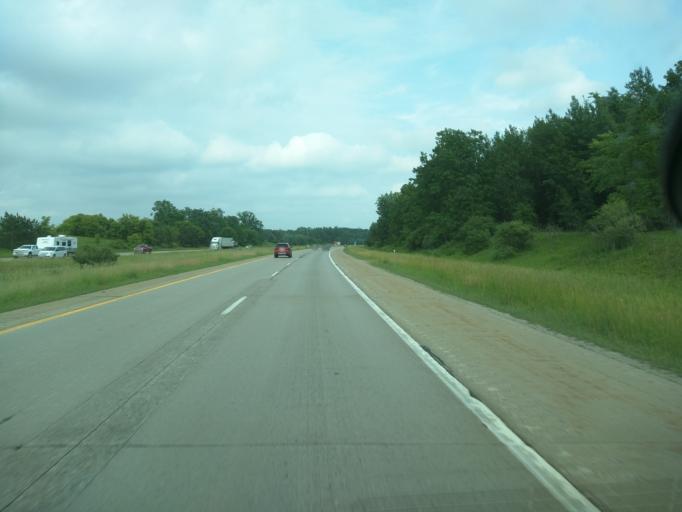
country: US
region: Michigan
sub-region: Clinton County
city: Bath
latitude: 42.8031
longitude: -84.4763
